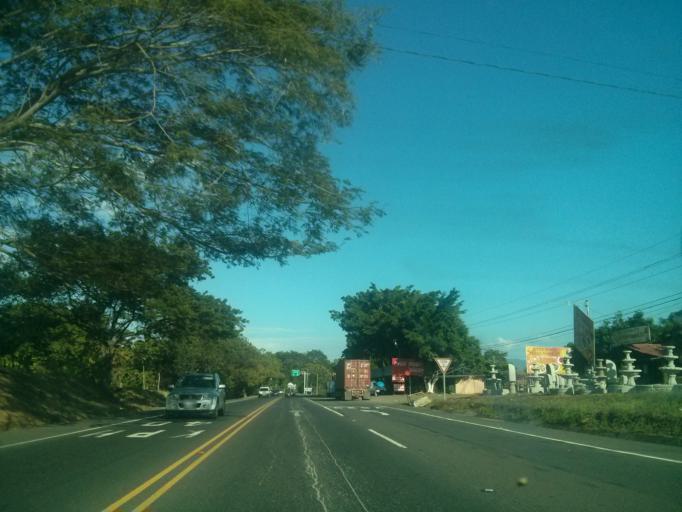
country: CR
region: Alajuela
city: Orotina
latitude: 9.8893
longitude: -84.5659
